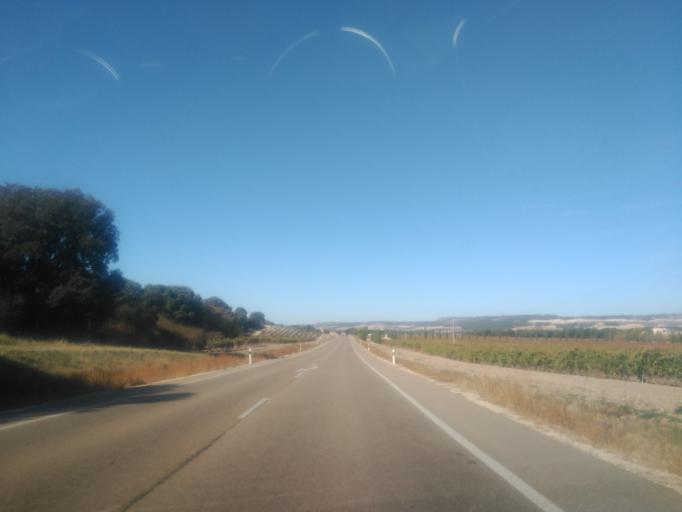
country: ES
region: Castille and Leon
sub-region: Provincia de Valladolid
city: Valbuena de Duero
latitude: 41.6254
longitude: -4.2765
